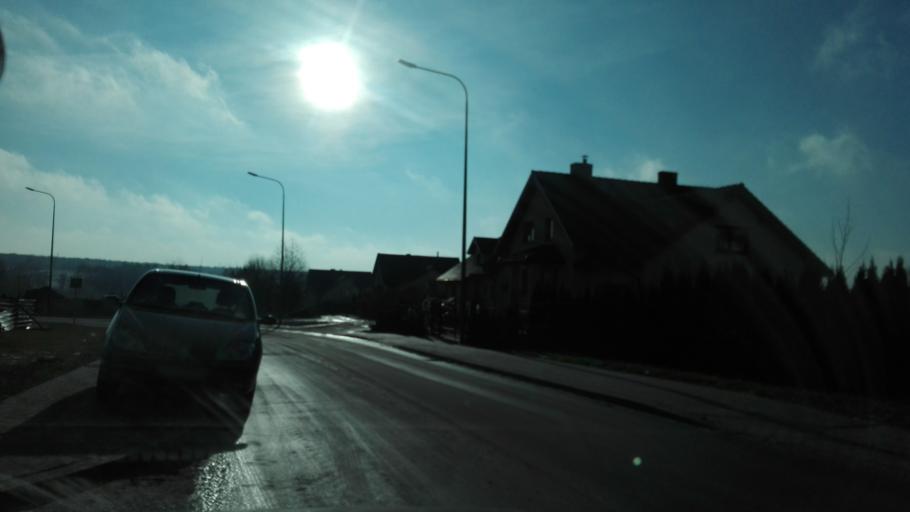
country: PL
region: Lublin Voivodeship
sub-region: Powiat lubelski
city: Kozubszczyzna
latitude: 51.2224
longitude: 22.4929
